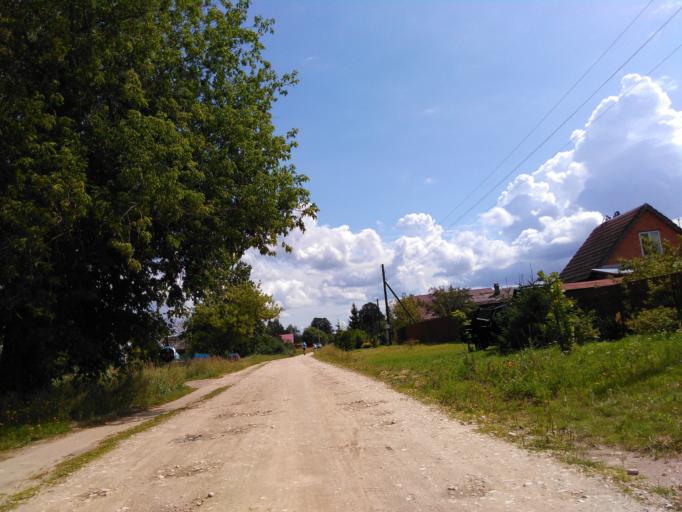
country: RU
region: Vladimir
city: Krasnyy Oktyabr'
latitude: 55.9991
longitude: 38.8528
